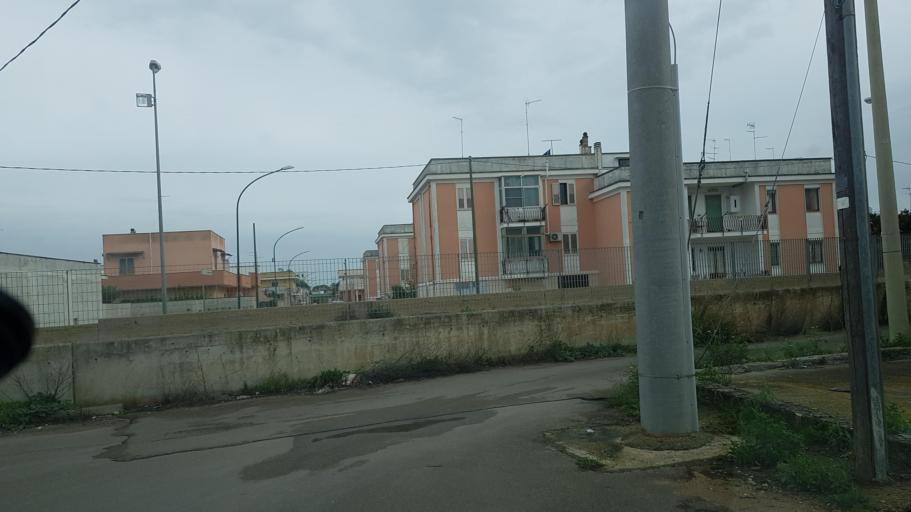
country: IT
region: Apulia
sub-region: Provincia di Lecce
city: Campi Salentina
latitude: 40.3926
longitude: 18.0218
